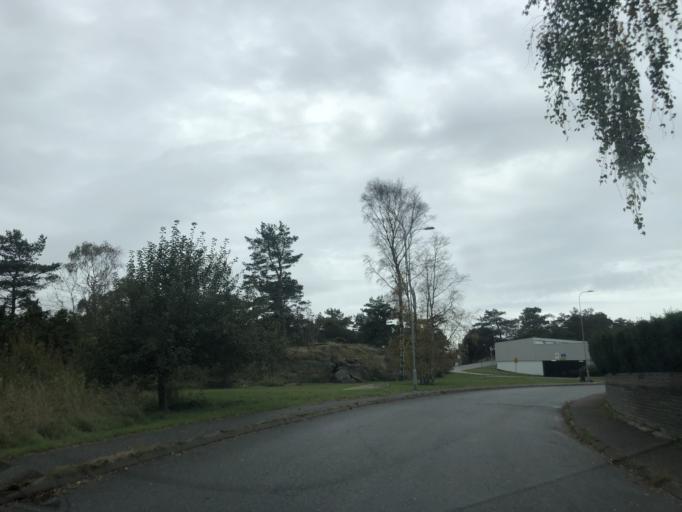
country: SE
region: Vaestra Goetaland
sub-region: Goteborg
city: Majorna
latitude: 57.6709
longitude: 11.8947
